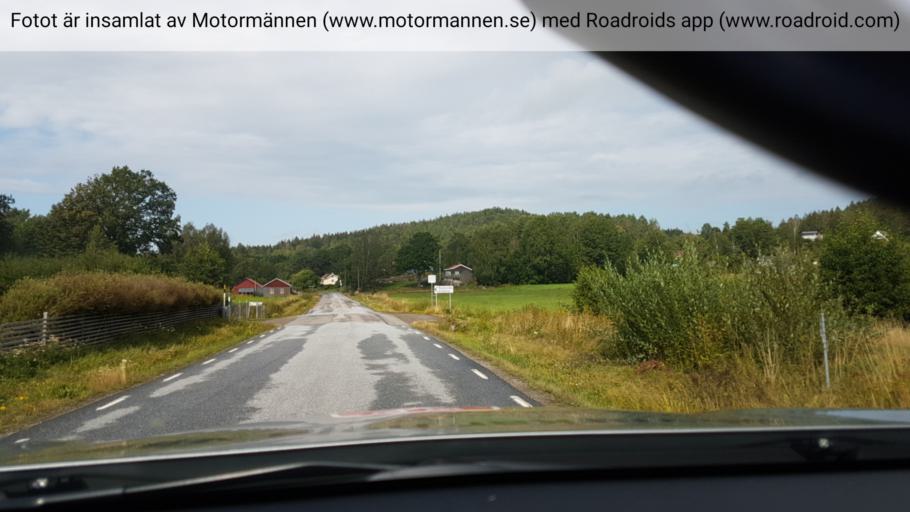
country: SE
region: Vaestra Goetaland
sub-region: Uddevalla Kommun
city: Ljungskile
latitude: 58.2340
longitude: 11.8777
